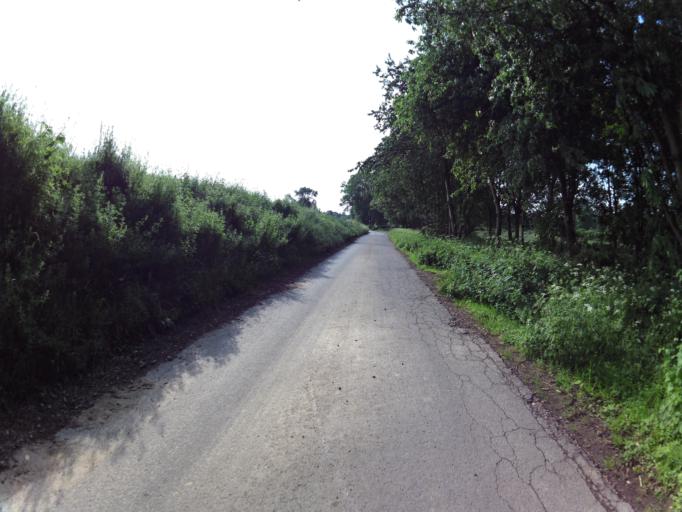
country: DE
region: North Rhine-Westphalia
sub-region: Regierungsbezirk Koln
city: Linnich
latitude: 50.9670
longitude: 6.2135
